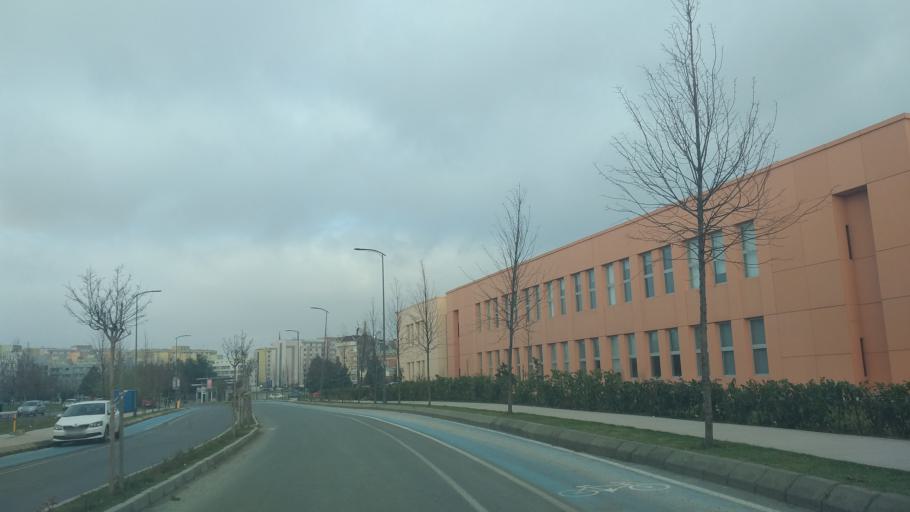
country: TR
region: Istanbul
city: merter keresteciler
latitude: 41.0289
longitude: 28.8924
